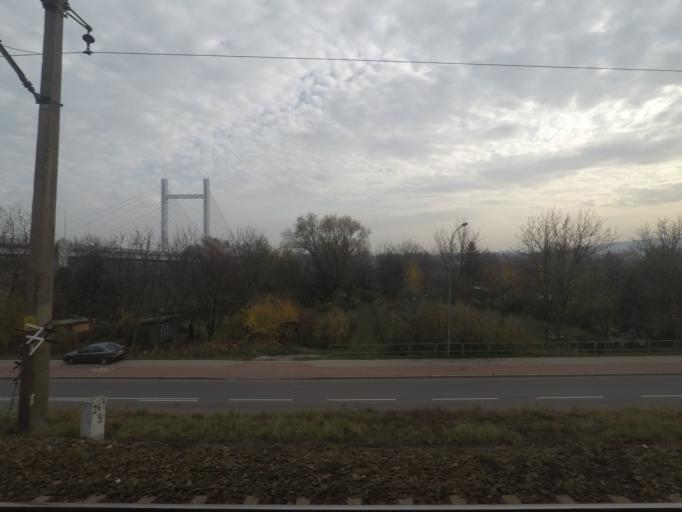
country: PL
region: Subcarpathian Voivodeship
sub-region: Przemysl
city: Przemysl
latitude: 49.7979
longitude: 22.7830
